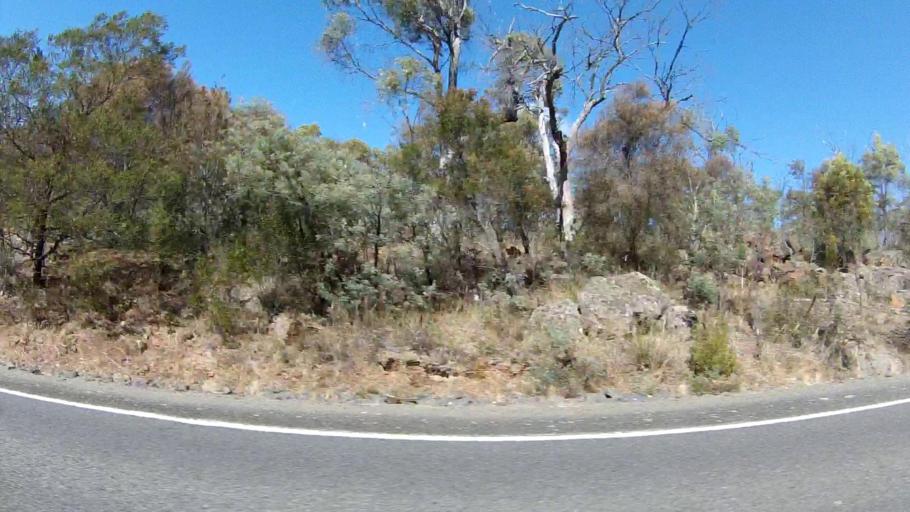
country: AU
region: Tasmania
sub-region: Sorell
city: Sorell
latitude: -42.5851
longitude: 147.8054
